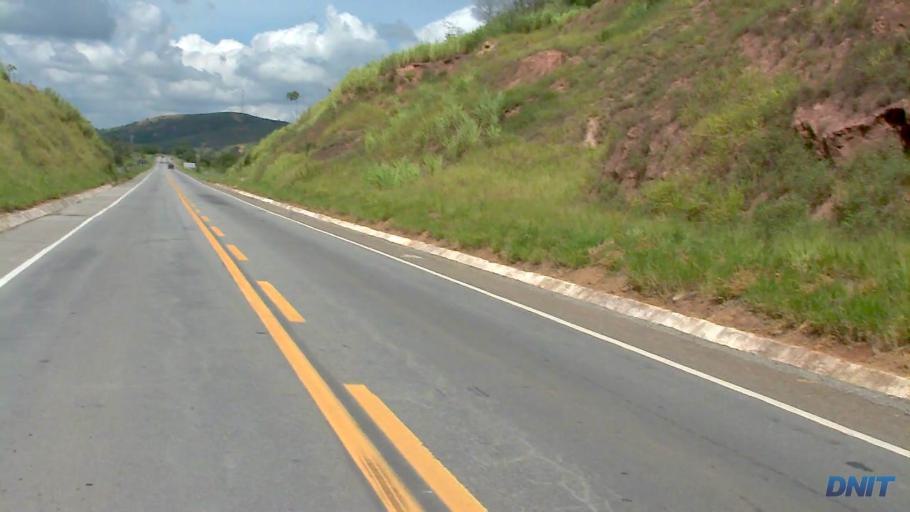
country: BR
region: Minas Gerais
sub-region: Governador Valadares
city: Governador Valadares
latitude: -19.0062
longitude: -42.1320
